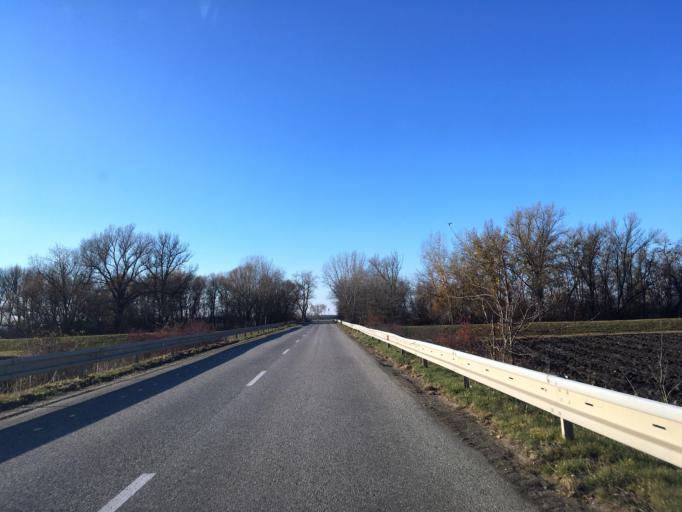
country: SK
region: Nitriansky
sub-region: Okres Komarno
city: Hurbanovo
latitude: 47.8939
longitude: 18.1884
